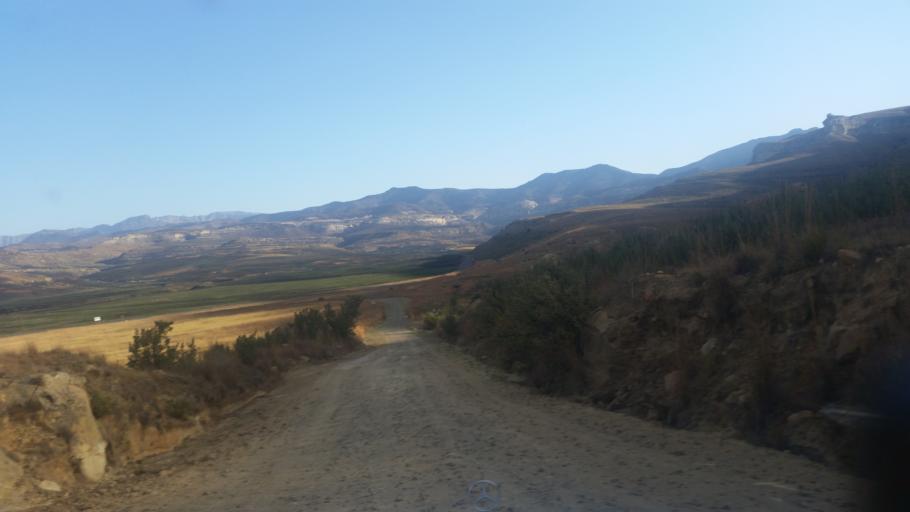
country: ZA
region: Orange Free State
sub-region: Thabo Mofutsanyana District Municipality
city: Phuthaditjhaba
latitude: -28.4990
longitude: 28.6864
